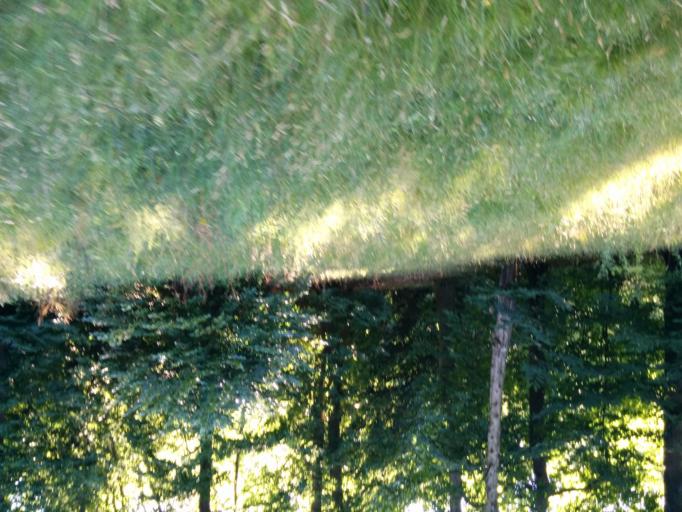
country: GB
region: England
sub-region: Surrey
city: Bramley
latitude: 51.1622
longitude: -0.5793
